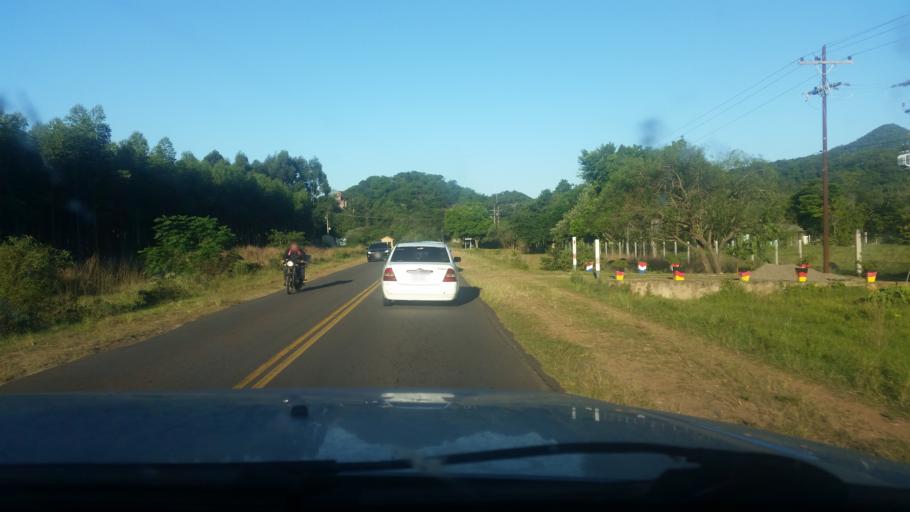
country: PY
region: Guaira
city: Independencia
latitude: -25.7257
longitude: -56.3011
